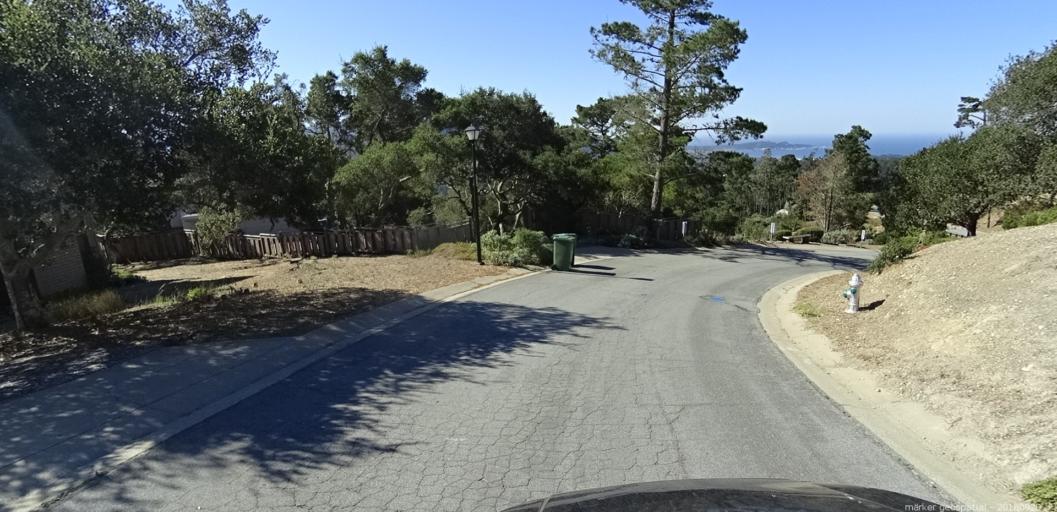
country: US
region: California
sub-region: Monterey County
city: Carmel-by-the-Sea
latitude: 36.5604
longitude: -121.8931
